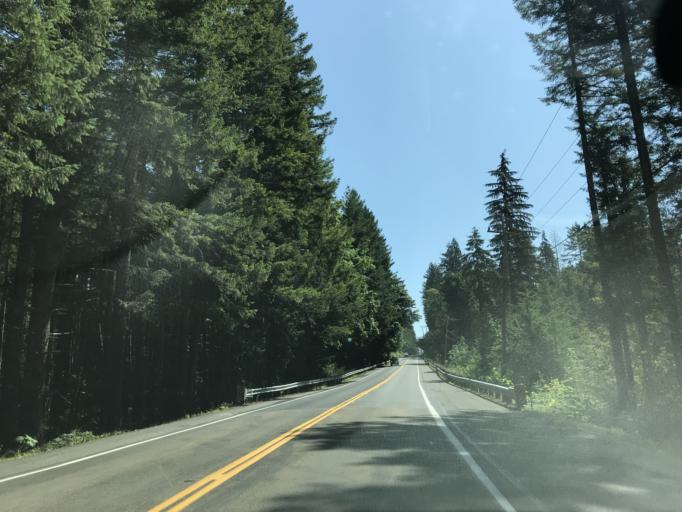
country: US
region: Washington
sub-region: King County
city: Ravensdale
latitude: 47.3580
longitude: -121.9433
